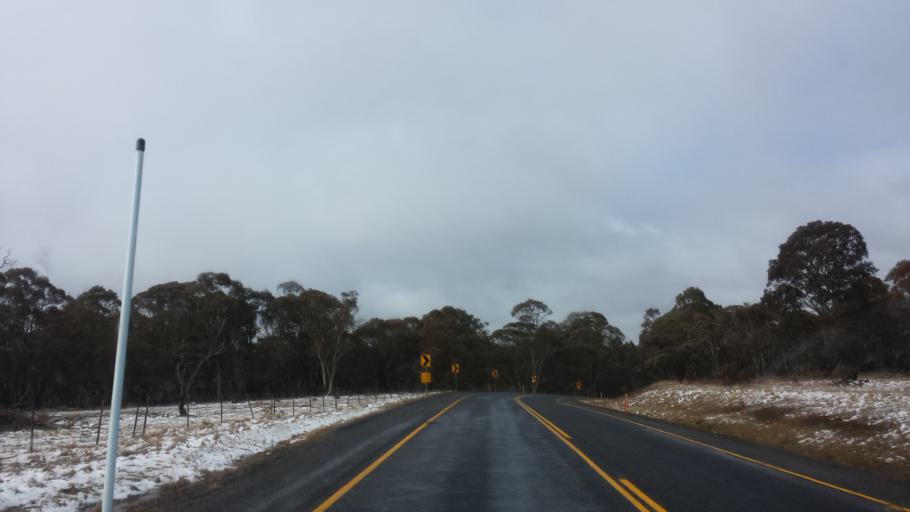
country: AU
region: Victoria
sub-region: Alpine
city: Mount Beauty
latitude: -37.0422
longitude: 147.3115
